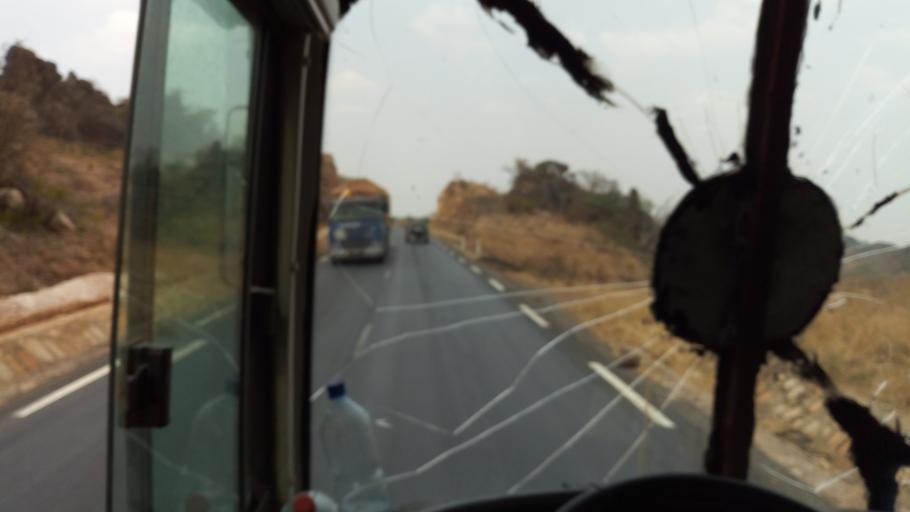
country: TG
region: Kara
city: Bafilo
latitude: 9.2714
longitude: 1.2362
